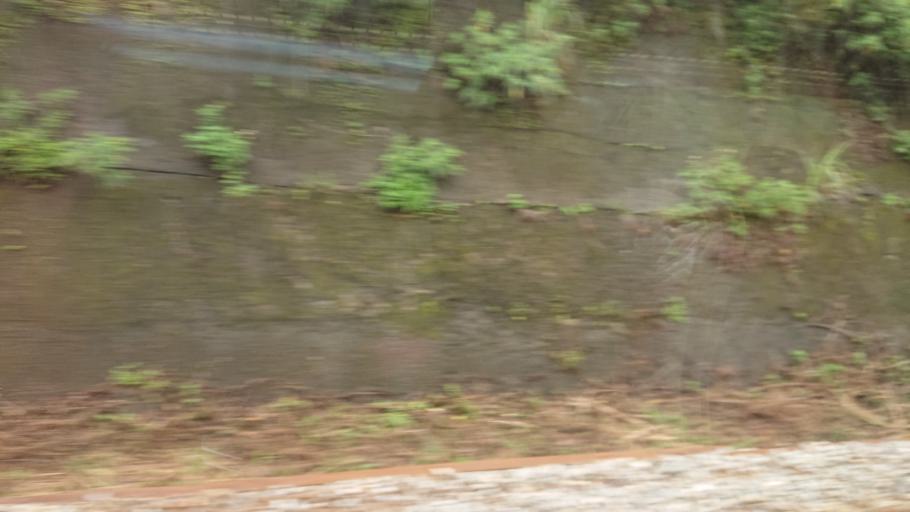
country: TW
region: Taiwan
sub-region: Keelung
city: Keelung
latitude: 25.0973
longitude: 121.8326
